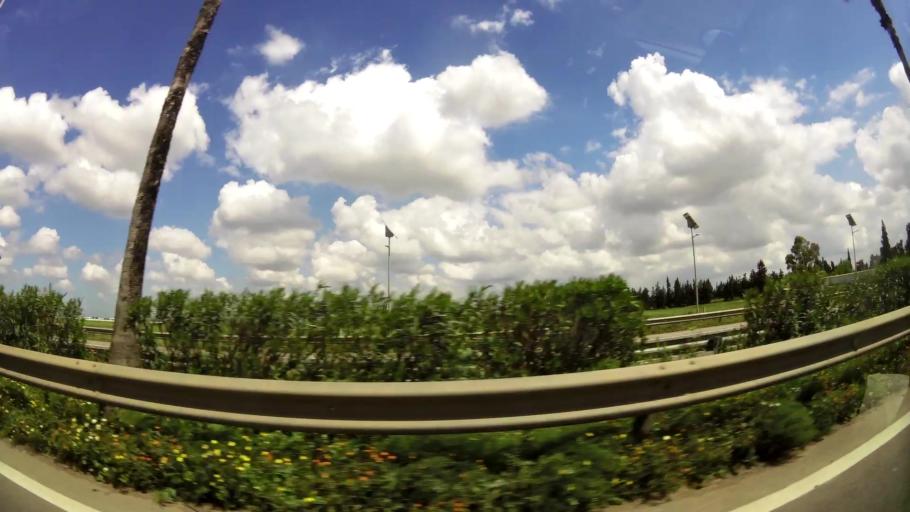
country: MA
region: Chaouia-Ouardigha
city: Nouaseur
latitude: 33.3992
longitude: -7.6212
